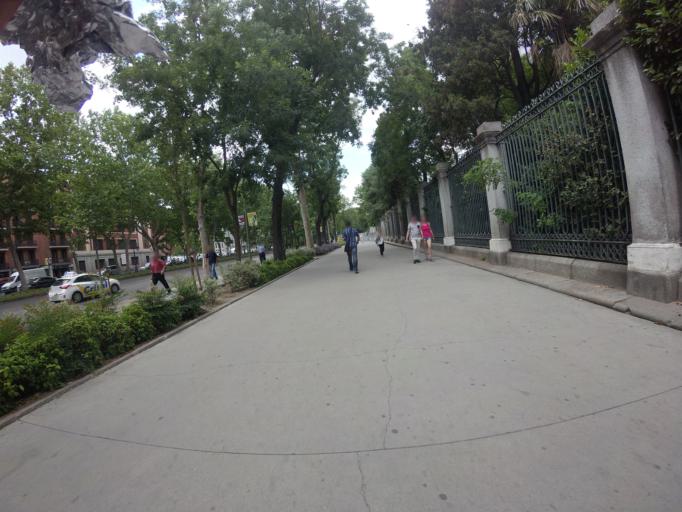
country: ES
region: Madrid
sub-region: Provincia de Madrid
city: Retiro
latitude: 40.4102
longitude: -3.6922
